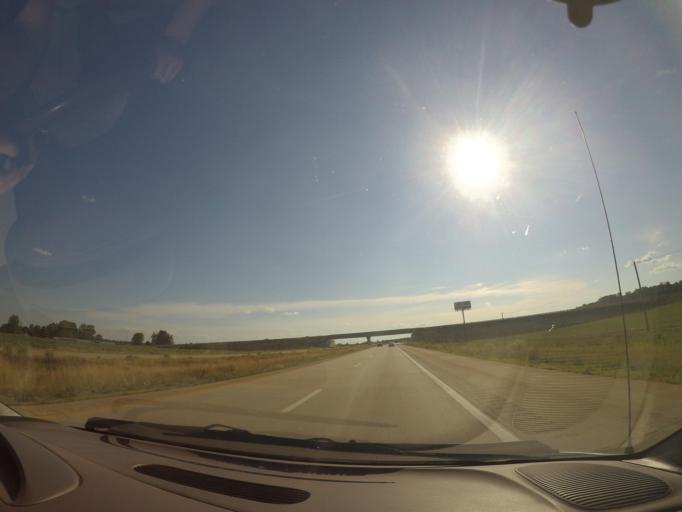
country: US
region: Ohio
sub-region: Lucas County
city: Whitehouse
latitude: 41.4347
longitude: -83.8709
